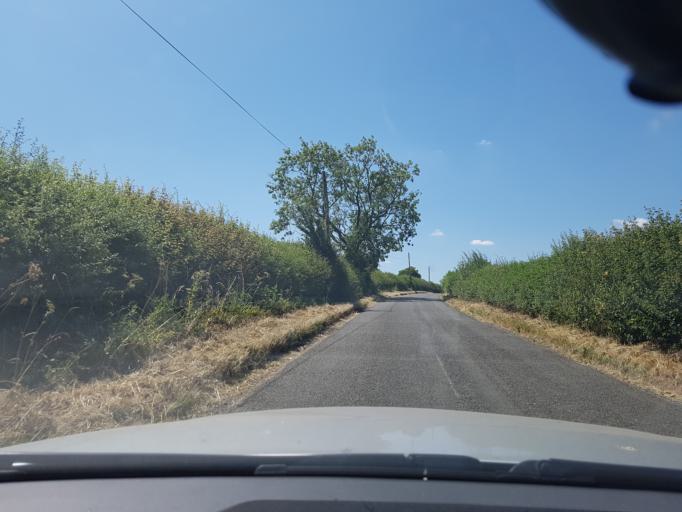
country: GB
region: England
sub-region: Northamptonshire
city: Deanshanger
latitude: 52.0216
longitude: -0.8897
